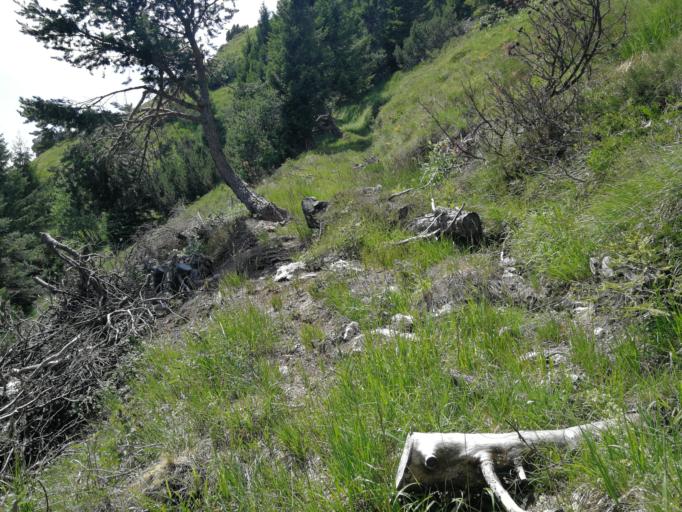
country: IT
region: Trentino-Alto Adige
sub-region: Provincia di Trento
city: Condino
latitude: 45.8658
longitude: 10.6131
